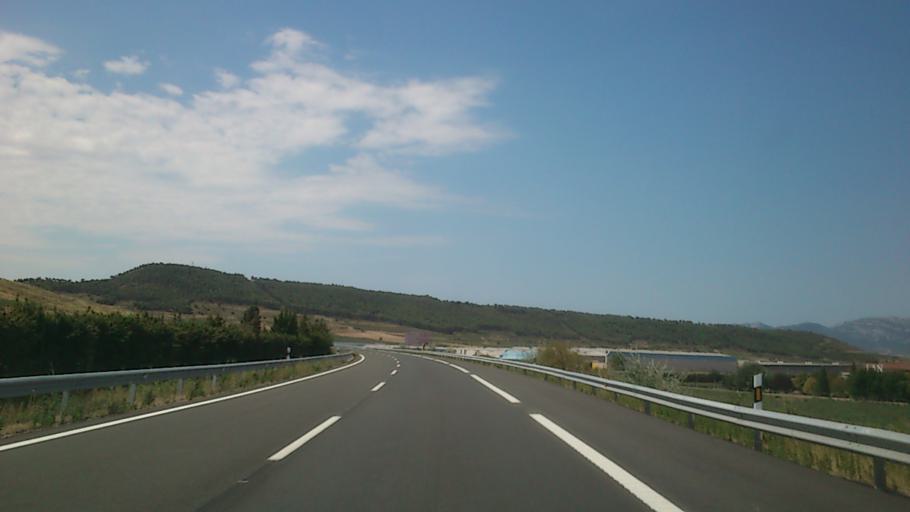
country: ES
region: La Rioja
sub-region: Provincia de La Rioja
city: Fuenmayor
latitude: 42.4622
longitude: -2.6019
